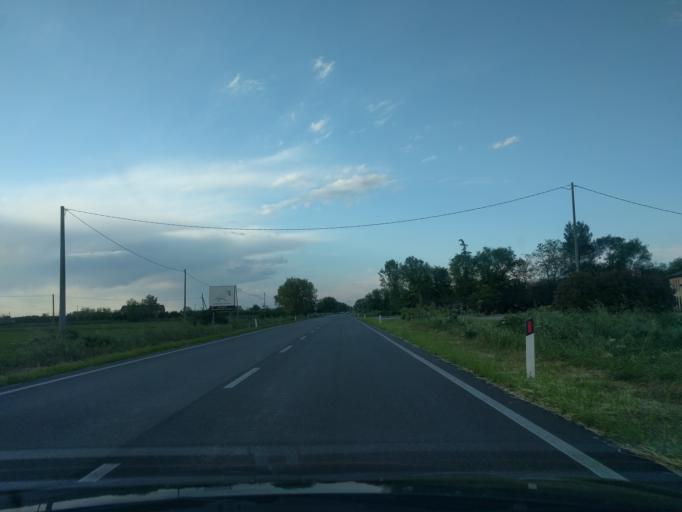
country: IT
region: Veneto
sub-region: Provincia di Rovigo
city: Polesella
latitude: 44.9466
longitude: 11.7352
